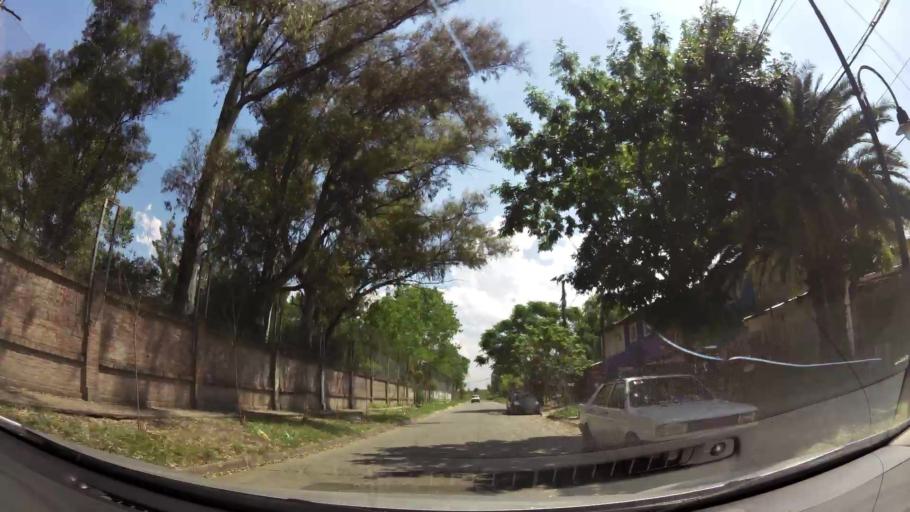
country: AR
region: Buenos Aires
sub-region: Partido de Tigre
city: Tigre
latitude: -34.4609
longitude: -58.5823
